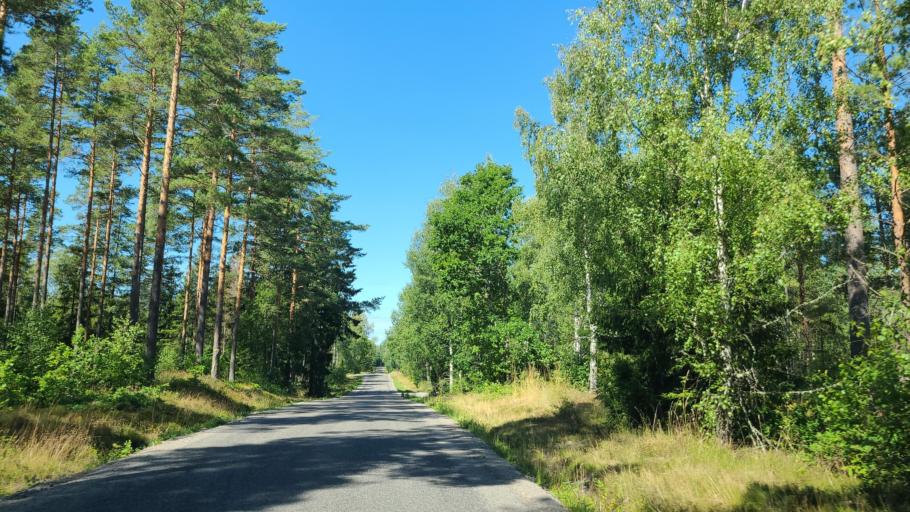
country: SE
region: Kalmar
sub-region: Kalmar Kommun
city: Ljungbyholm
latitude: 56.5691
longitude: 16.0538
